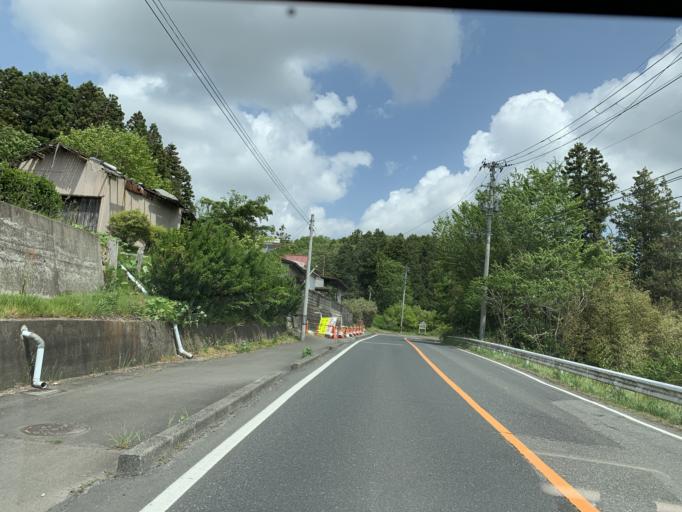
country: JP
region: Miyagi
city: Kogota
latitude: 38.6542
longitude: 141.0579
